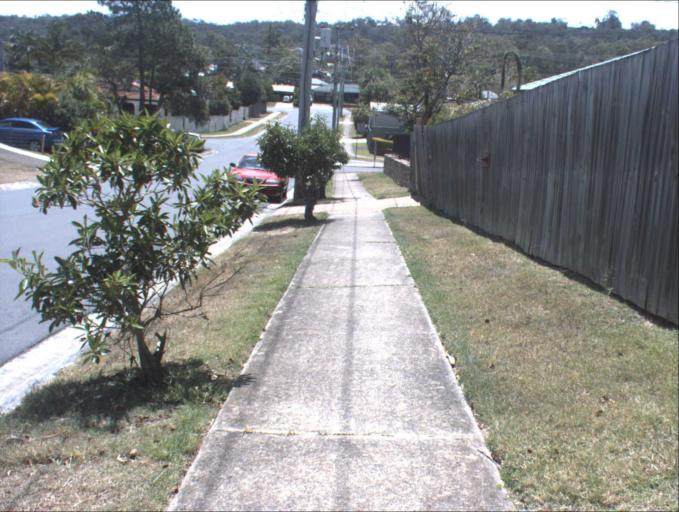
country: AU
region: Queensland
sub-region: Logan
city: Slacks Creek
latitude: -27.6362
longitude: 153.1453
